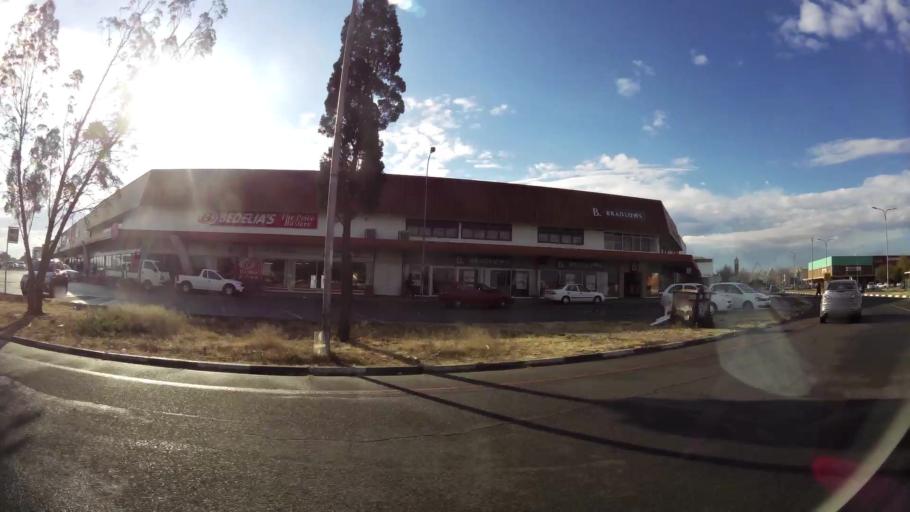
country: ZA
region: Orange Free State
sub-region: Lejweleputswa District Municipality
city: Welkom
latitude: -27.9855
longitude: 26.7354
